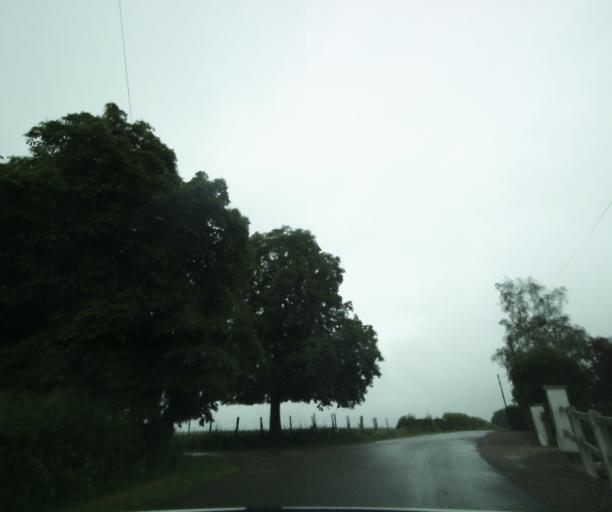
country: FR
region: Bourgogne
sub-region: Departement de Saone-et-Loire
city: Charolles
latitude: 46.4536
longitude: 4.2104
